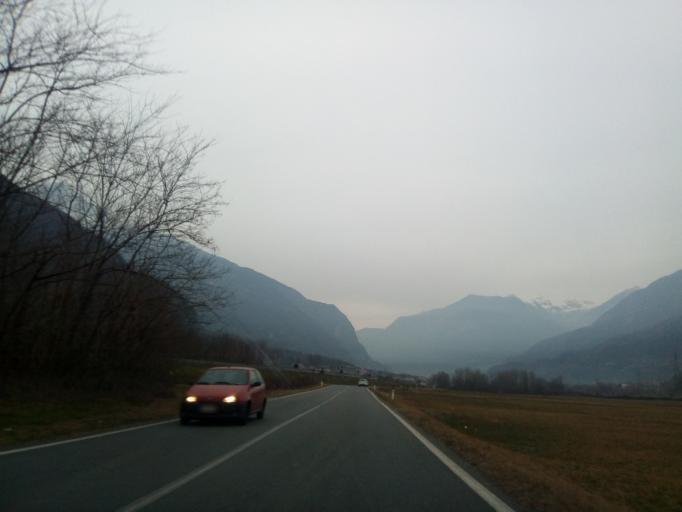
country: IT
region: Piedmont
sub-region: Provincia di Torino
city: Tavagnasco
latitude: 45.5365
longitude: 7.8305
